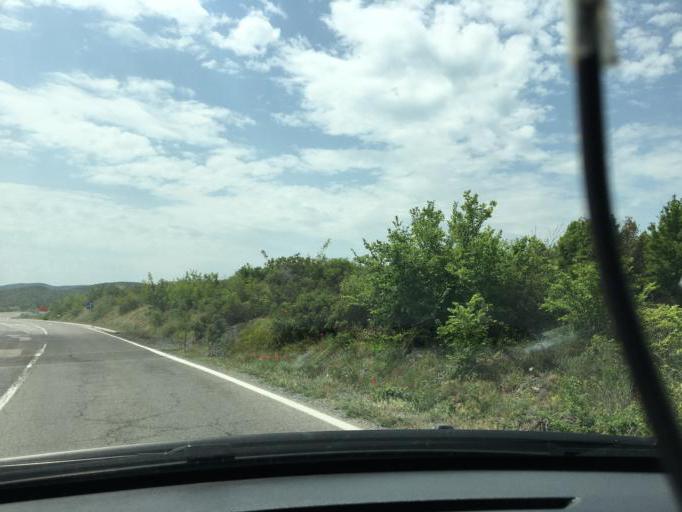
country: MK
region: Gevgelija
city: Miravci
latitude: 41.2667
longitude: 22.4763
